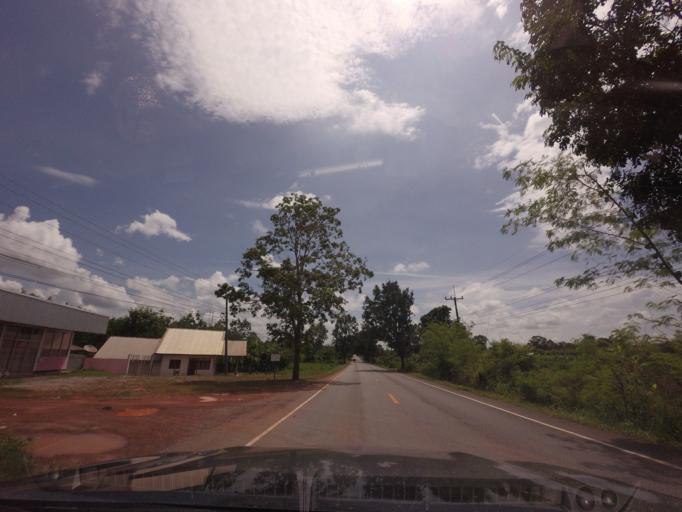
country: TH
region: Nong Khai
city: Pho Tak
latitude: 17.7972
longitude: 102.3516
